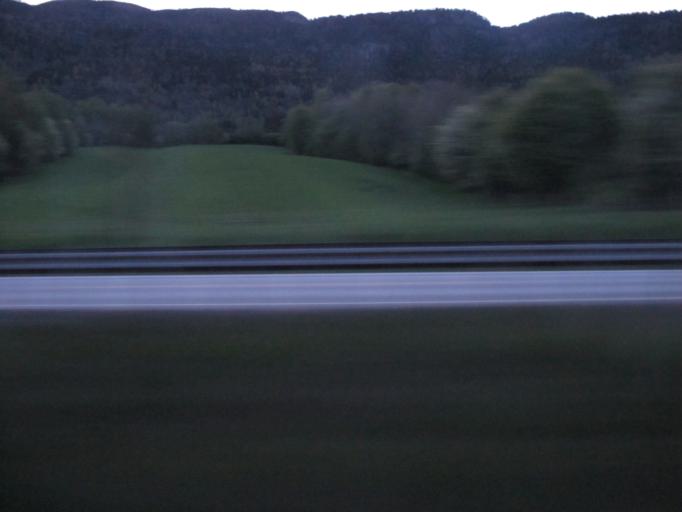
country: NO
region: Oppland
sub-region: Nord-Fron
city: Vinstra
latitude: 61.6628
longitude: 9.7270
